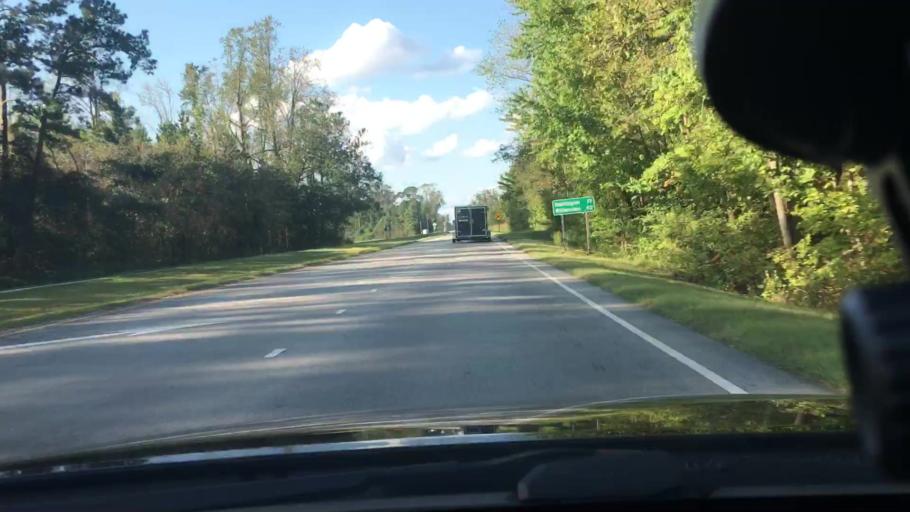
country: US
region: North Carolina
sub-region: Craven County
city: Vanceboro
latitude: 35.2892
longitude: -77.1289
